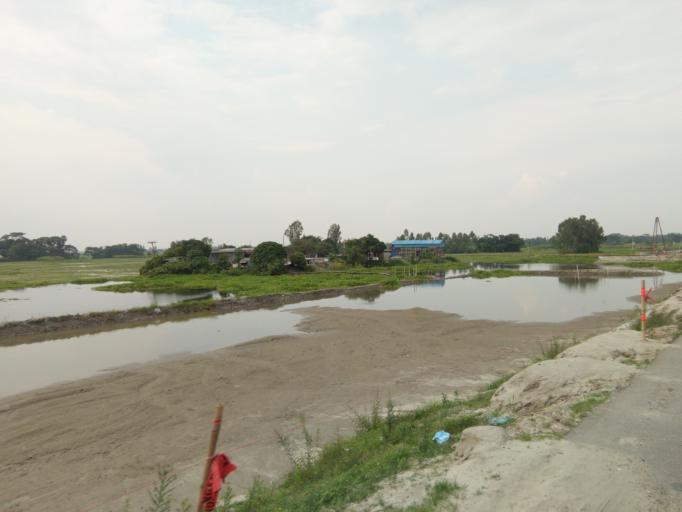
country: BD
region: Dhaka
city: Dohar
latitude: 23.5653
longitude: 90.2991
